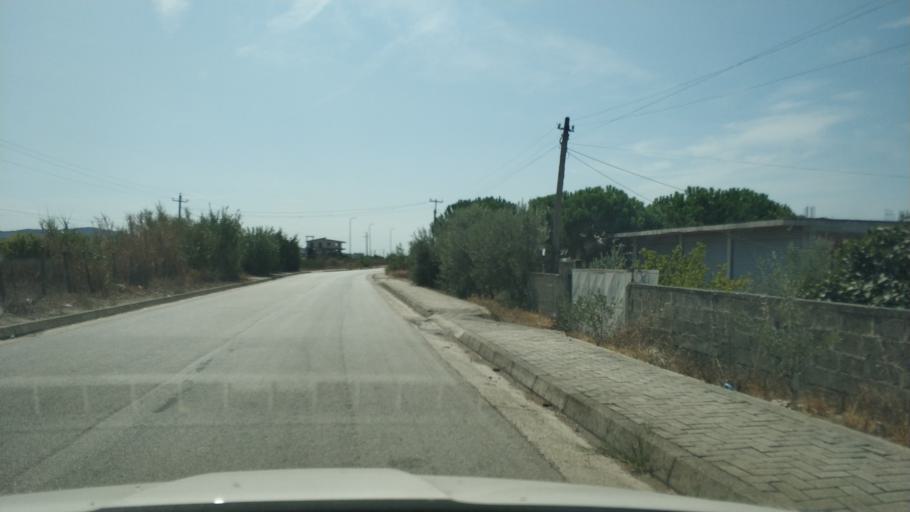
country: AL
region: Fier
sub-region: Rrethi i Lushnjes
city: Divjake
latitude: 40.9869
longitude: 19.5345
